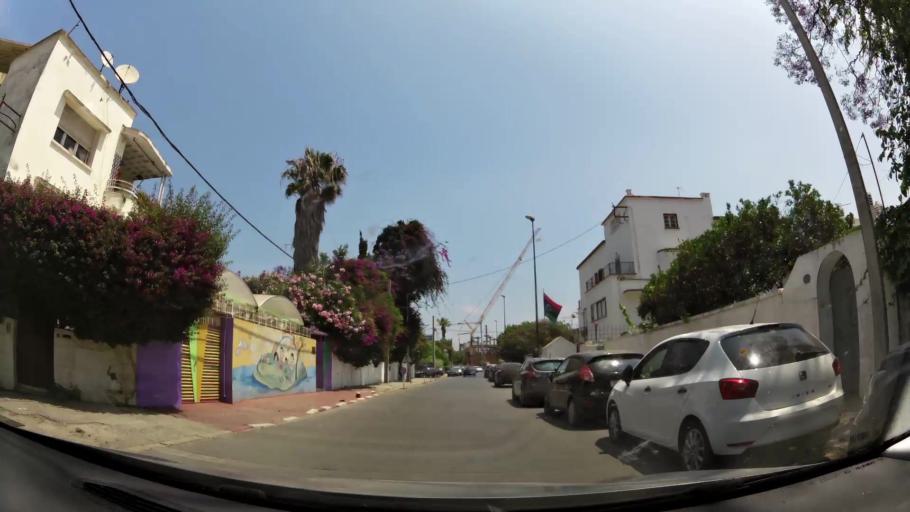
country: MA
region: Rabat-Sale-Zemmour-Zaer
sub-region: Rabat
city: Rabat
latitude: 34.0144
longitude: -6.8402
